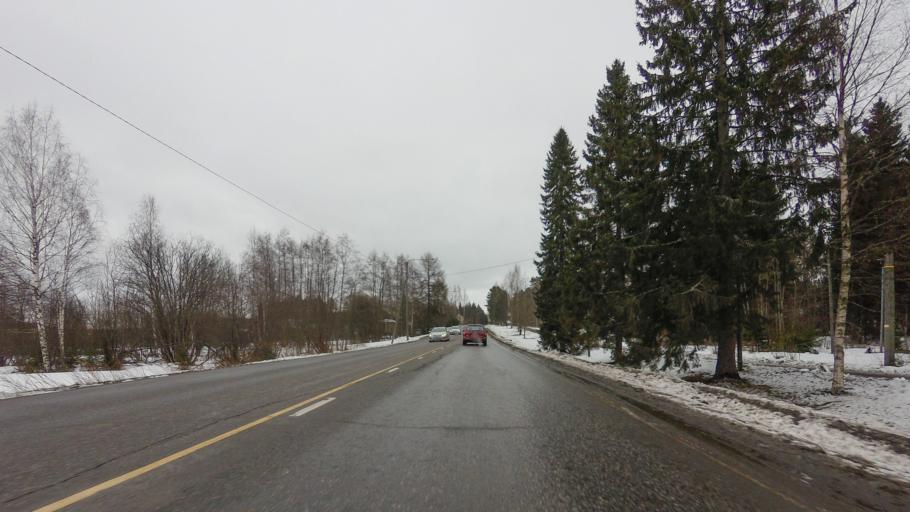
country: FI
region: Southern Savonia
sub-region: Savonlinna
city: Savonlinna
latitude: 61.8824
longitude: 28.9424
